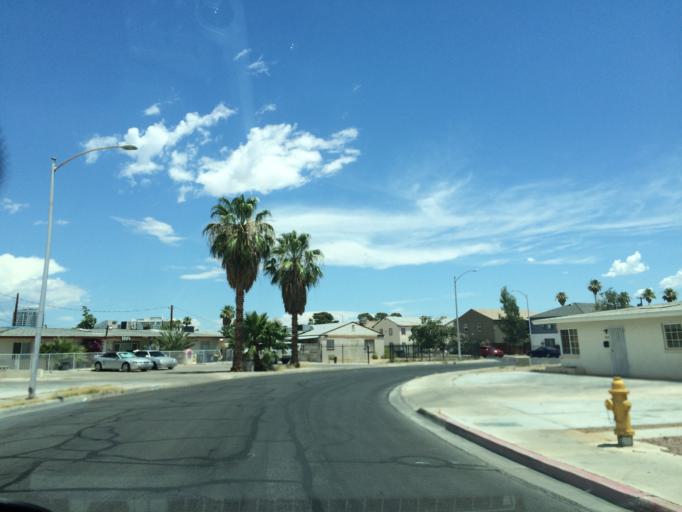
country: US
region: Nevada
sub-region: Clark County
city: Las Vegas
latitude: 36.1496
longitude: -115.1517
